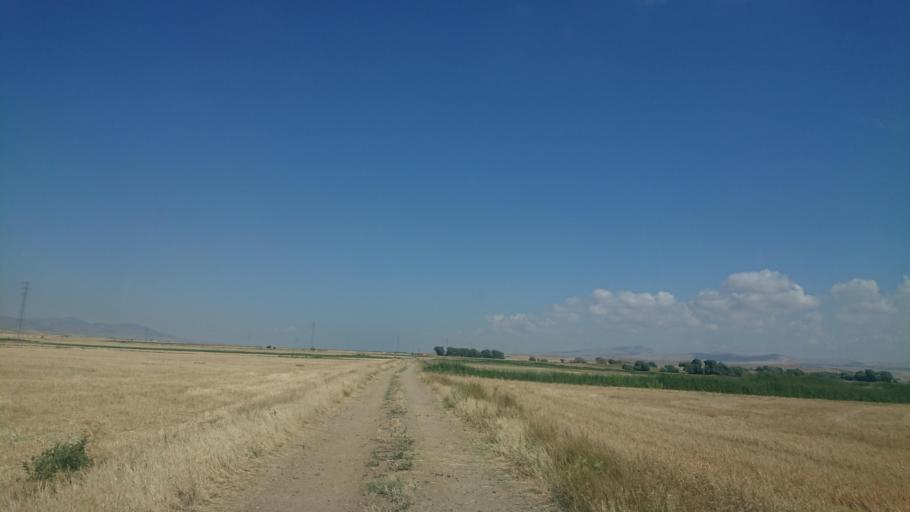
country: TR
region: Aksaray
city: Sariyahsi
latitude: 38.9900
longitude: 33.9007
